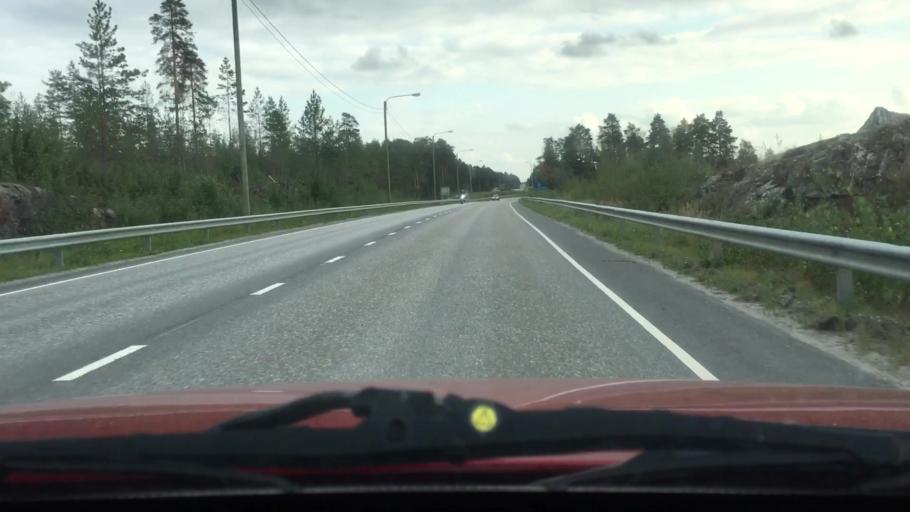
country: FI
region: Varsinais-Suomi
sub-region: Turku
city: Masku
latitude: 60.5459
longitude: 22.1275
